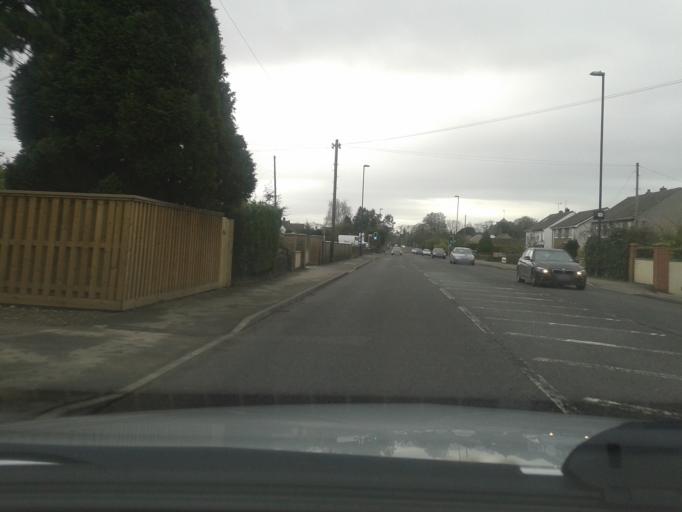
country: GB
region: England
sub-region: South Gloucestershire
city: Winterbourne
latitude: 51.5270
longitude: -2.4679
